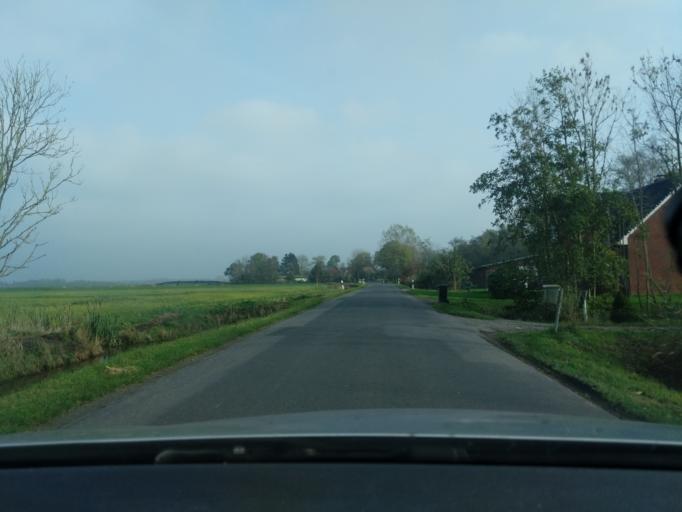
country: DE
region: Lower Saxony
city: Neuenkirchen
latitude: 53.7369
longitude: 8.8759
